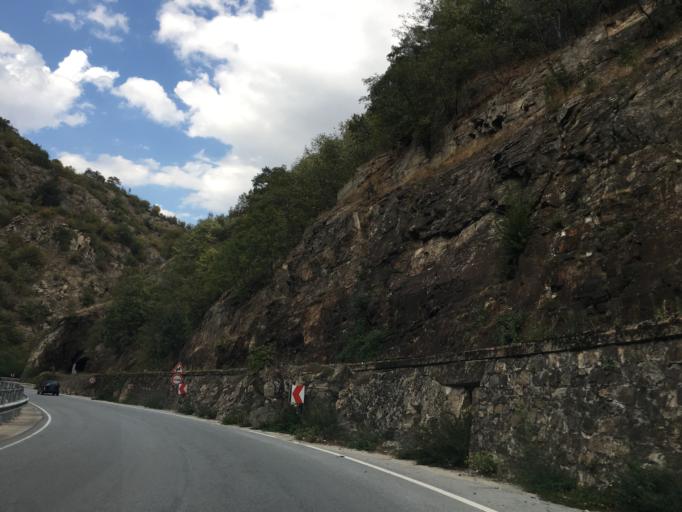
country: BG
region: Pazardzhik
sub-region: Obshtina Septemvri
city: Septemvri
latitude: 42.1215
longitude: 24.1199
